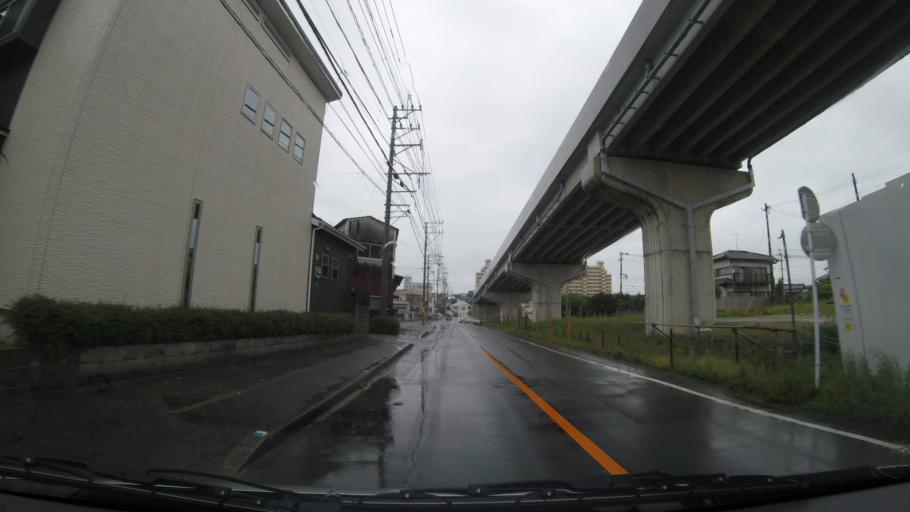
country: JP
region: Fukuoka
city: Koga
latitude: 33.7238
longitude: 130.4601
